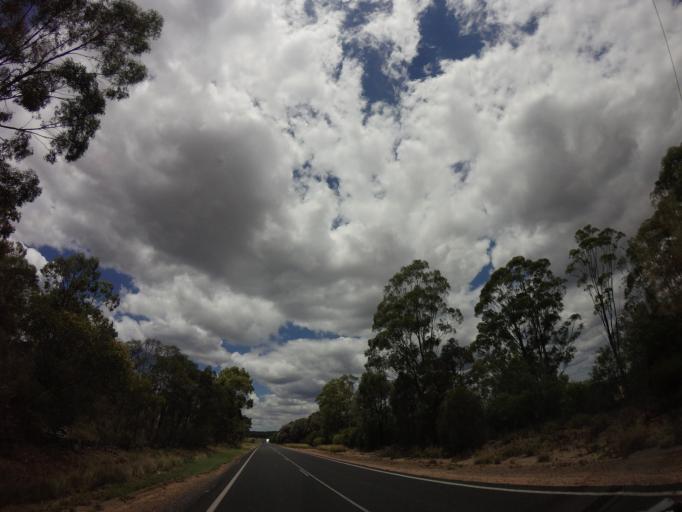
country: AU
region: Queensland
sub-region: Goondiwindi
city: Goondiwindi
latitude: -28.0023
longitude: 150.9068
